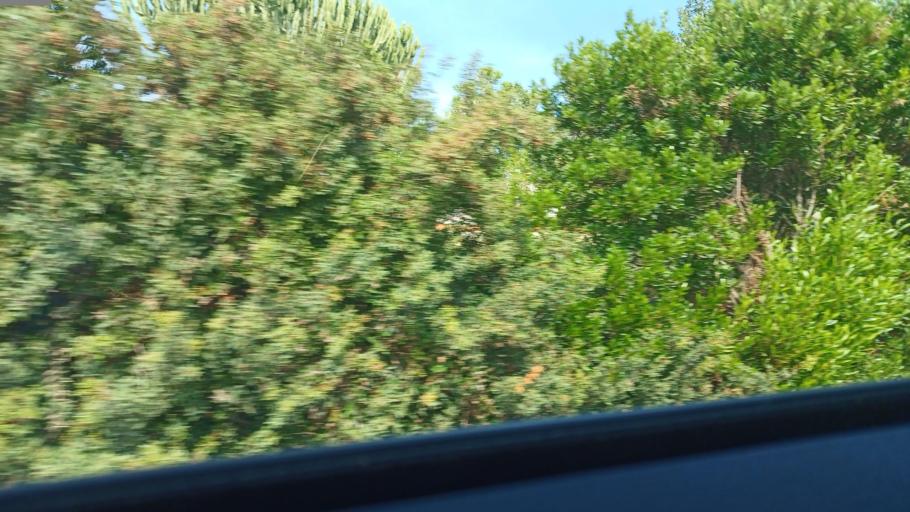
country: CY
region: Pafos
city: Pegeia
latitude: 34.8806
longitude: 32.3754
